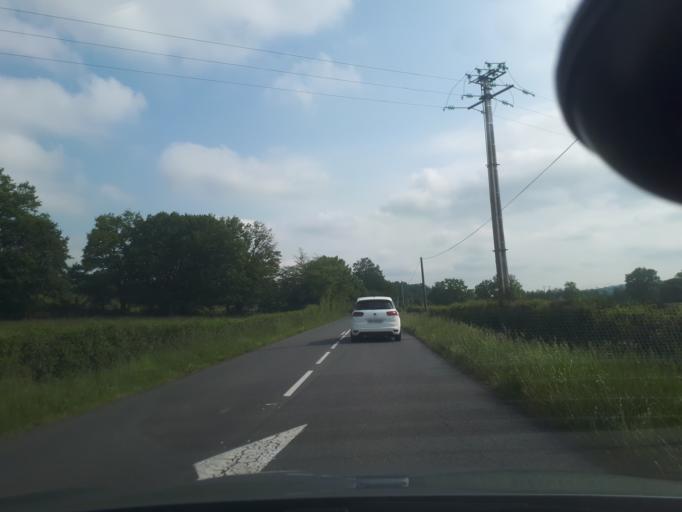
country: FR
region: Auvergne
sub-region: Departement de l'Allier
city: Dompierre-sur-Besbre
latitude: 46.4079
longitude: 3.6035
